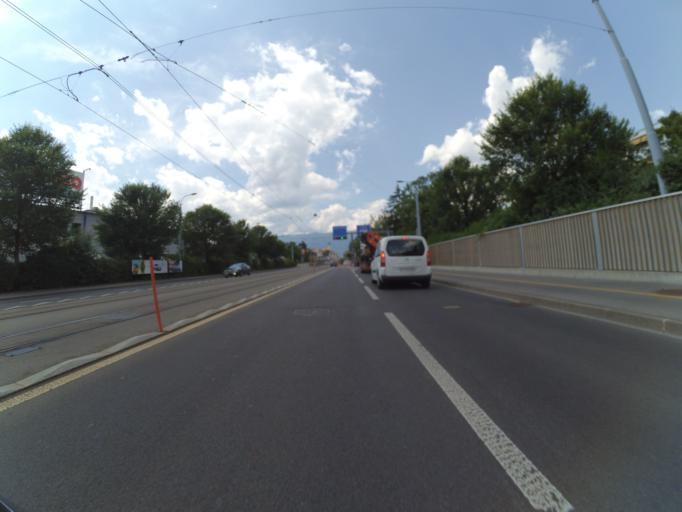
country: CH
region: Geneva
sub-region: Geneva
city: Meyrin
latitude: 46.2276
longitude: 6.0767
